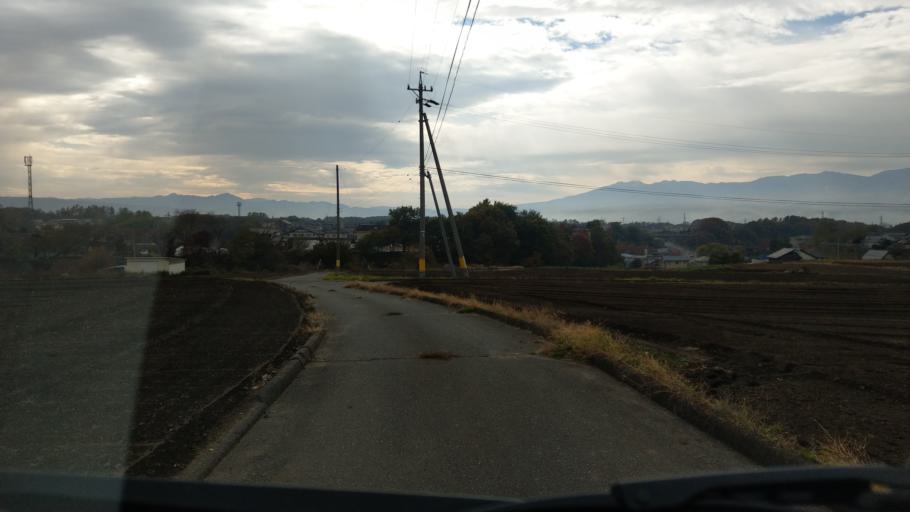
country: JP
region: Nagano
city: Komoro
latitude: 36.3185
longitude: 138.4590
